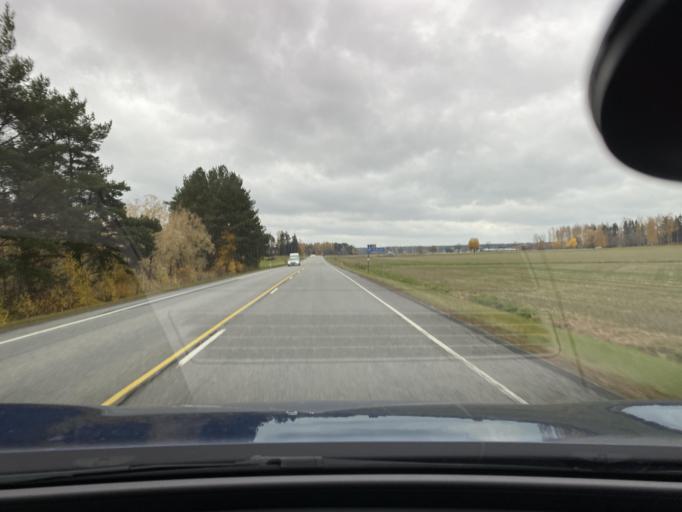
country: FI
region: Satakunta
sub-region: Rauma
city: Kiukainen
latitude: 61.1892
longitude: 22.0604
